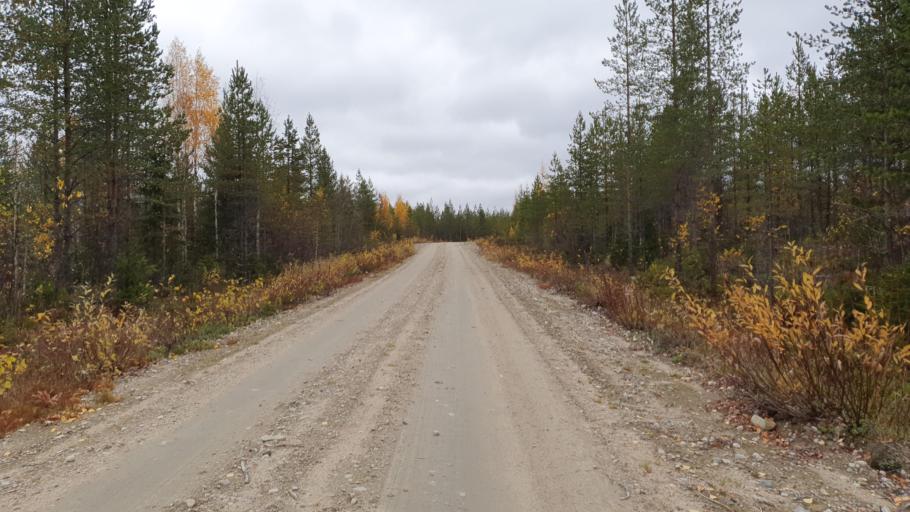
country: FI
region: Kainuu
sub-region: Kehys-Kainuu
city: Kuhmo
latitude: 64.4545
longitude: 29.6066
